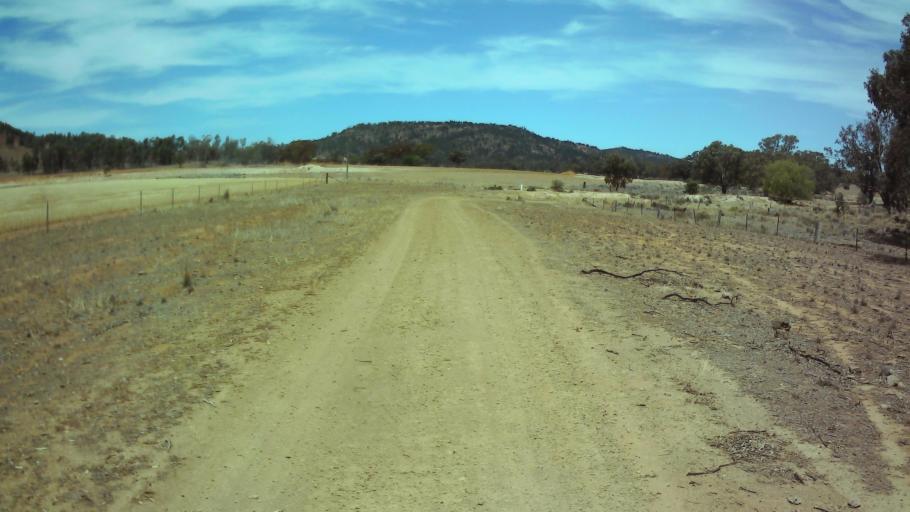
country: AU
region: New South Wales
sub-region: Weddin
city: Grenfell
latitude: -33.7595
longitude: 148.1447
